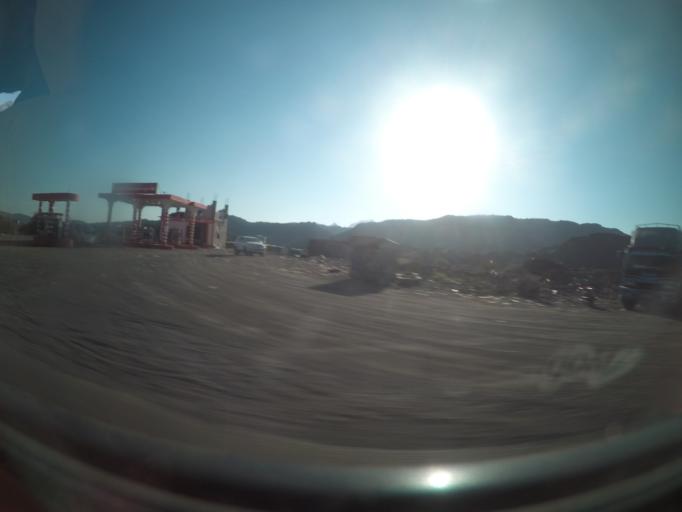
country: YE
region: Lahij
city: Habil ar Raydah
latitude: 13.6587
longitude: 44.8417
